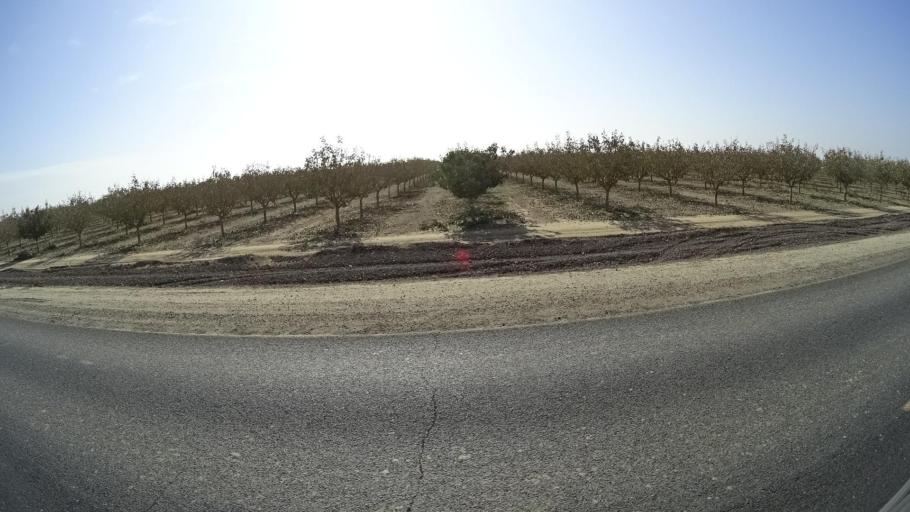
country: US
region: California
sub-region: Kern County
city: McFarland
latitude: 35.6020
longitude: -119.1844
